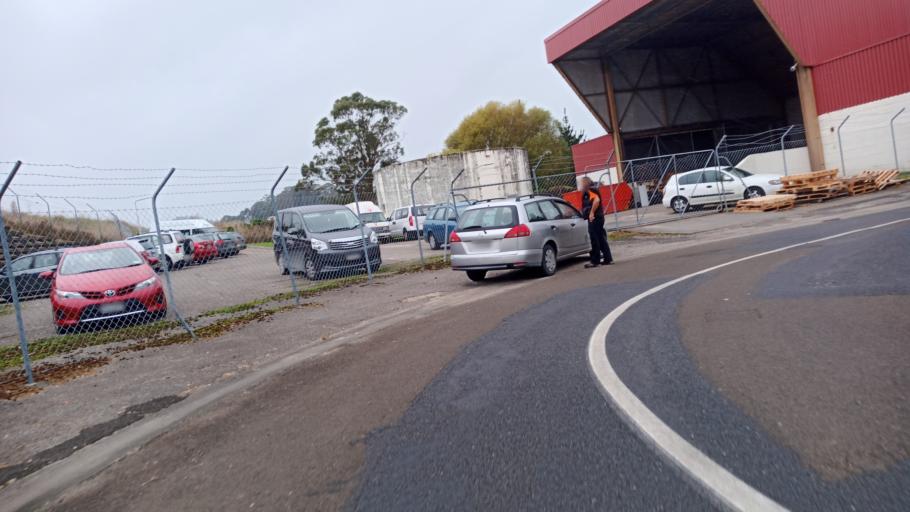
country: NZ
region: Gisborne
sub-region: Gisborne District
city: Gisborne
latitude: -38.6375
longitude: 178.0070
